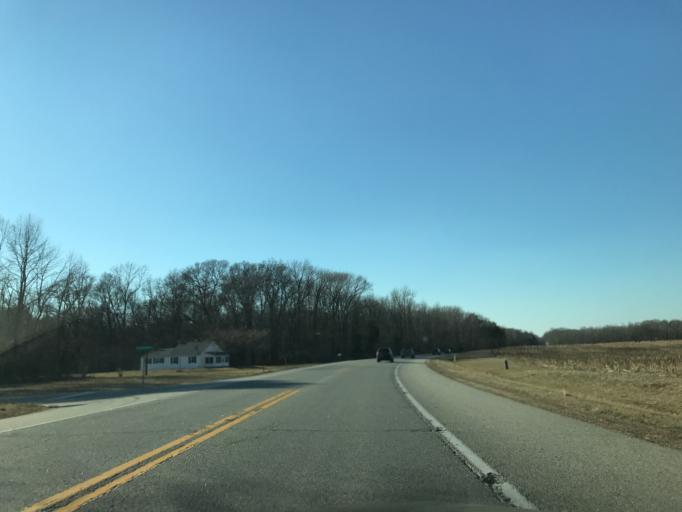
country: US
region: Maryland
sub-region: Caroline County
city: Greensboro
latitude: 39.0466
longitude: -75.8281
